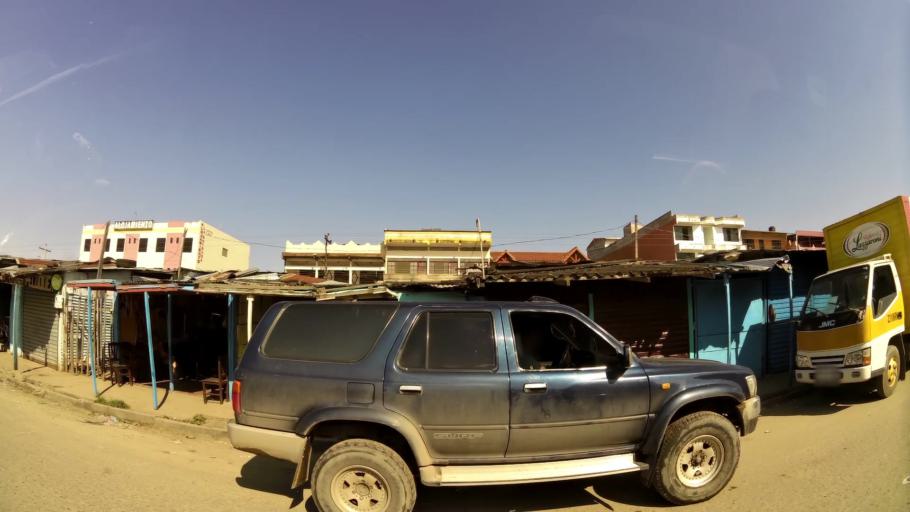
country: BO
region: Santa Cruz
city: Santa Cruz de la Sierra
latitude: -17.8246
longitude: -63.1309
